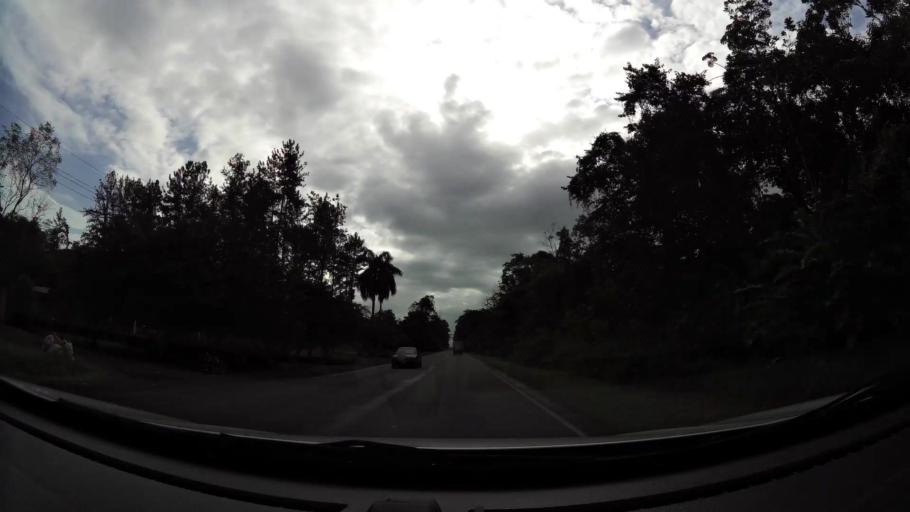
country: CR
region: Limon
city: Pocora
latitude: 10.1827
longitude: -83.6266
